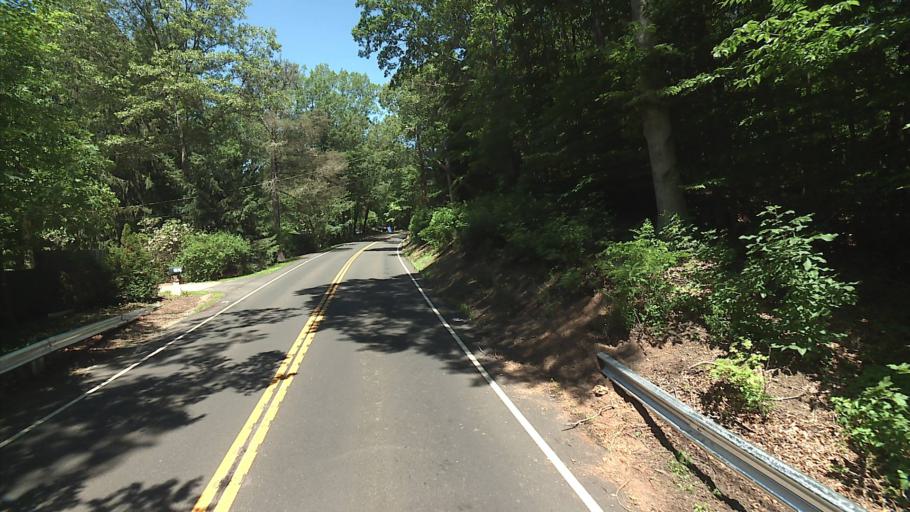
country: US
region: Connecticut
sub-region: New Haven County
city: Guilford
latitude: 41.3370
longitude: -72.7094
